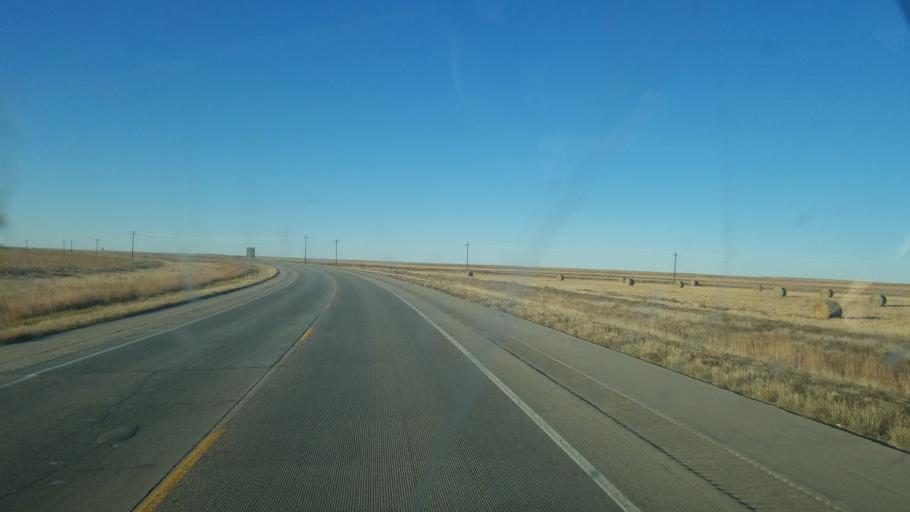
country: US
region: Colorado
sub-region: Kiowa County
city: Eads
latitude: 38.6821
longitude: -102.7834
